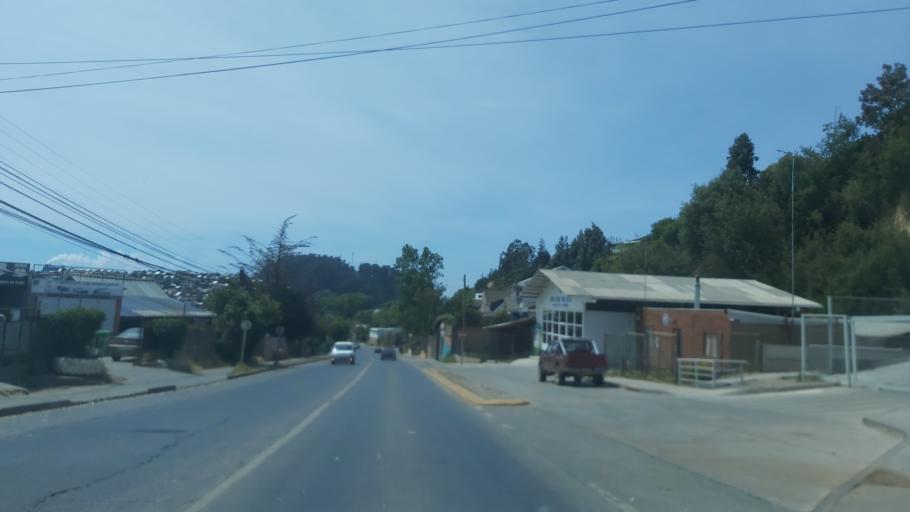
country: CL
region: Maule
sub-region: Provincia de Talca
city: Constitucion
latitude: -35.3365
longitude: -72.4169
